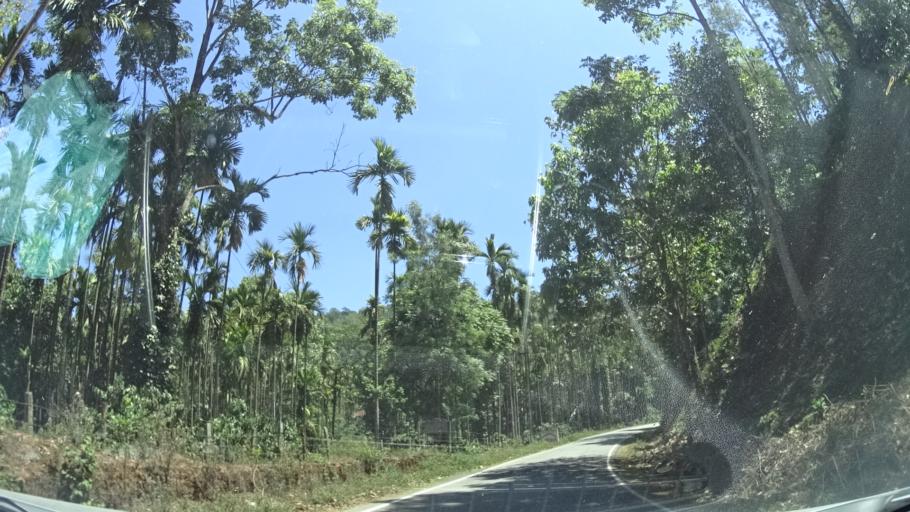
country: IN
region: Karnataka
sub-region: Chikmagalur
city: Sringeri
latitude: 13.2063
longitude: 75.3370
